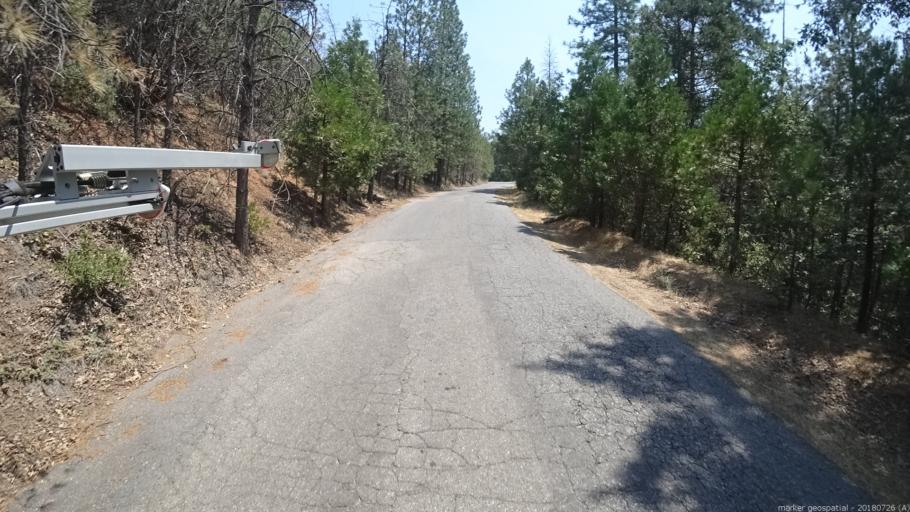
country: US
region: California
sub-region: Madera County
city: Oakhurst
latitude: 37.2772
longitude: -119.6287
